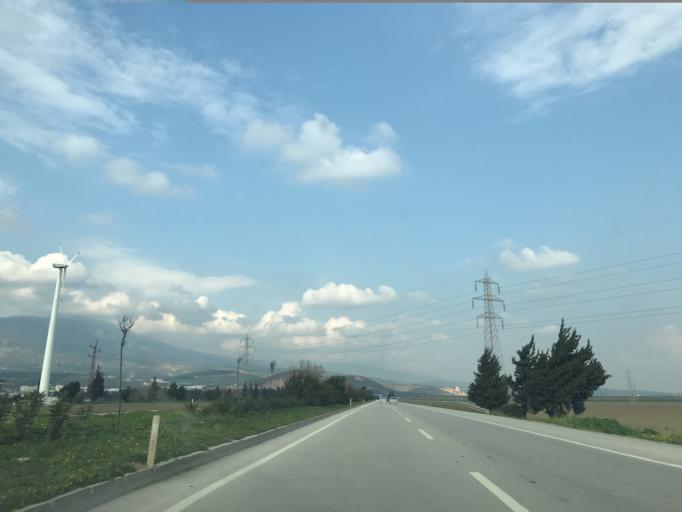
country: TR
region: Hatay
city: Serinyol
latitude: 36.4158
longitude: 36.2720
